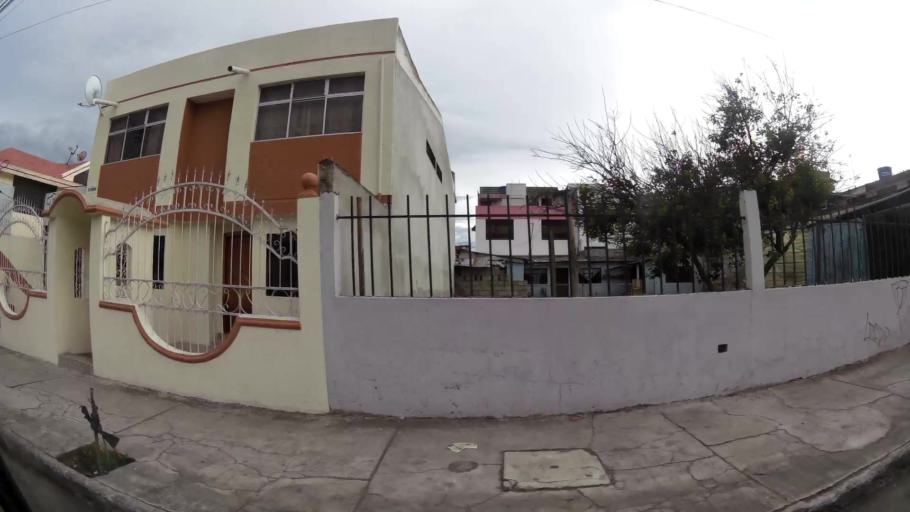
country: EC
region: Tungurahua
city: Ambato
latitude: -1.2708
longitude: -78.6238
